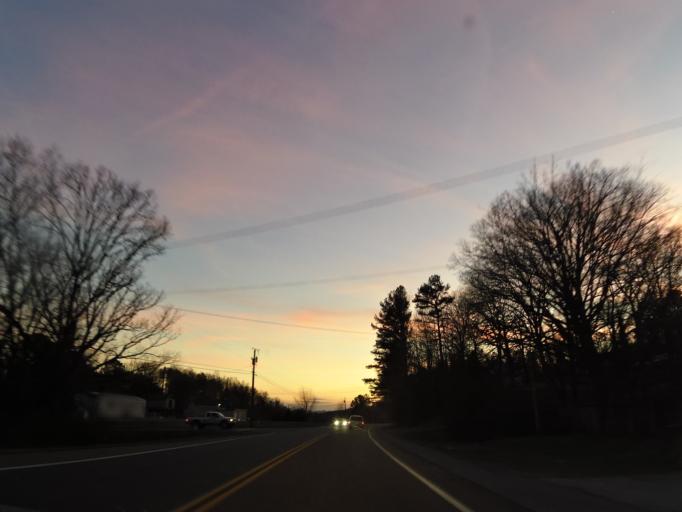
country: US
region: Tennessee
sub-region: Hamilton County
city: Apison
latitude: 34.9980
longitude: -84.9253
